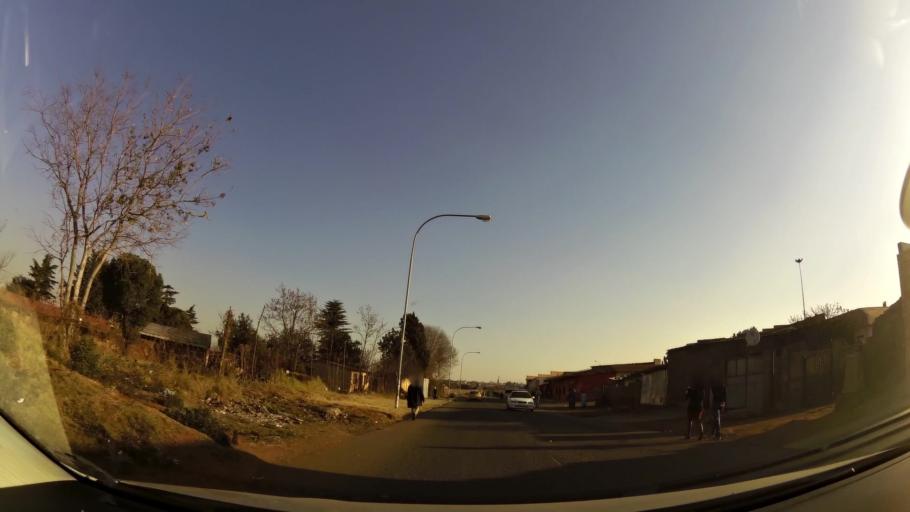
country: ZA
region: Gauteng
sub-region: City of Johannesburg Metropolitan Municipality
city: Soweto
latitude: -26.2569
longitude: 27.8788
